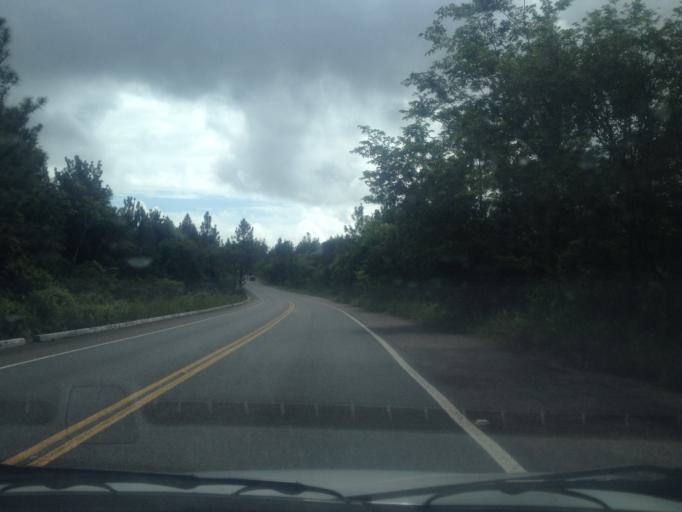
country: BR
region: Bahia
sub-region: Entre Rios
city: Entre Rios
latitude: -12.1400
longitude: -37.7915
